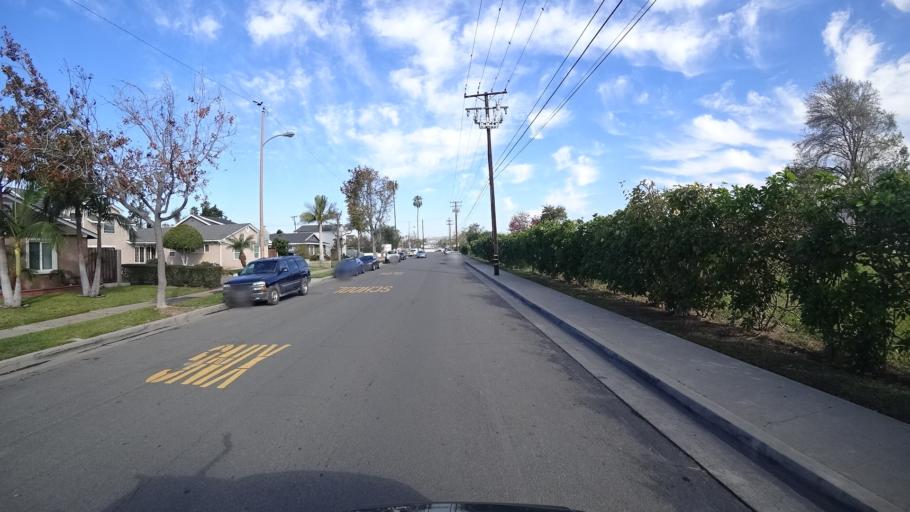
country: US
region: California
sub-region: Orange County
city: Villa Park
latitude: 33.7934
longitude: -117.8101
